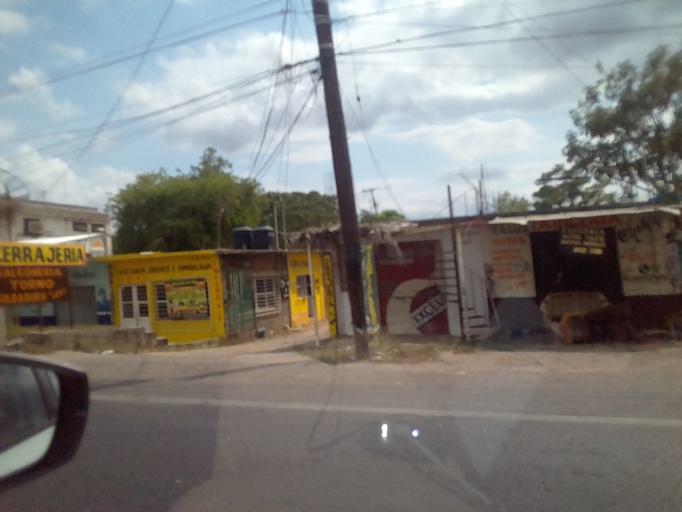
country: MX
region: Oaxaca
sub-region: Santo Domingo Tehuantepec
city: Santo Domingo Tehuantepec
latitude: 16.3140
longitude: -95.2373
